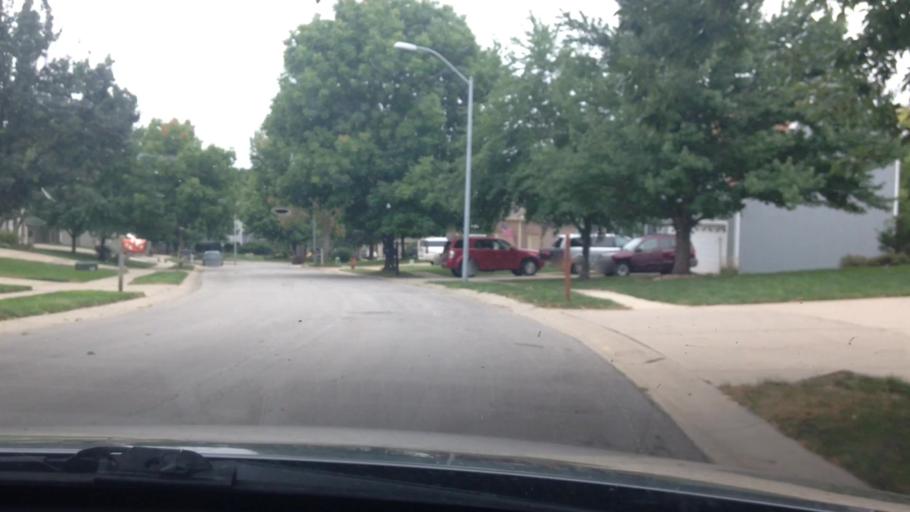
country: US
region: Missouri
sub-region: Platte County
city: Weatherby Lake
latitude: 39.2369
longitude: -94.6511
